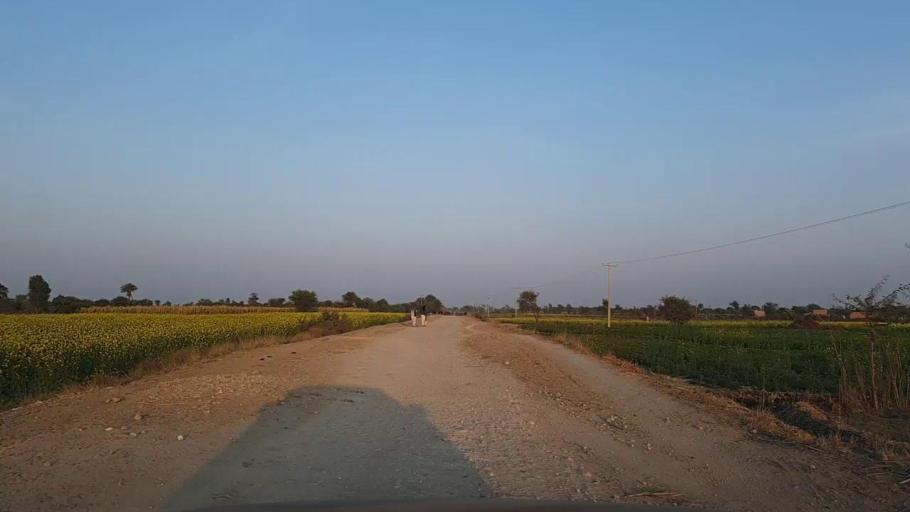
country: PK
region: Sindh
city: Tando Mittha Khan
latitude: 25.9693
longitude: 69.0827
